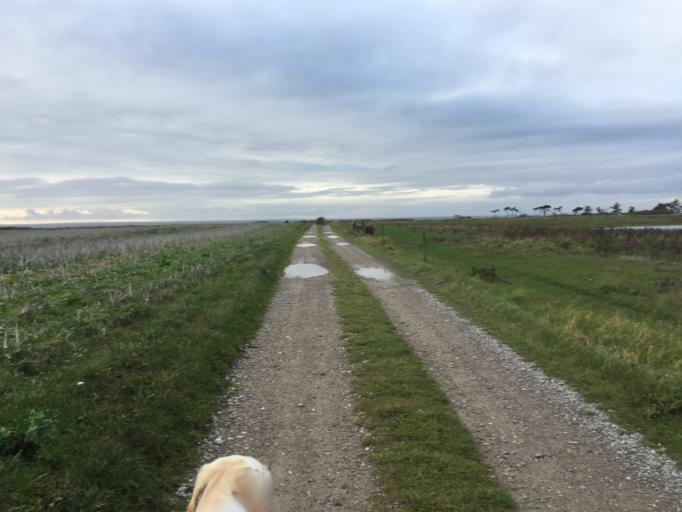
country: DK
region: Zealand
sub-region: Slagelse Kommune
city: Skaelskor
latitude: 55.2069
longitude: 11.1787
